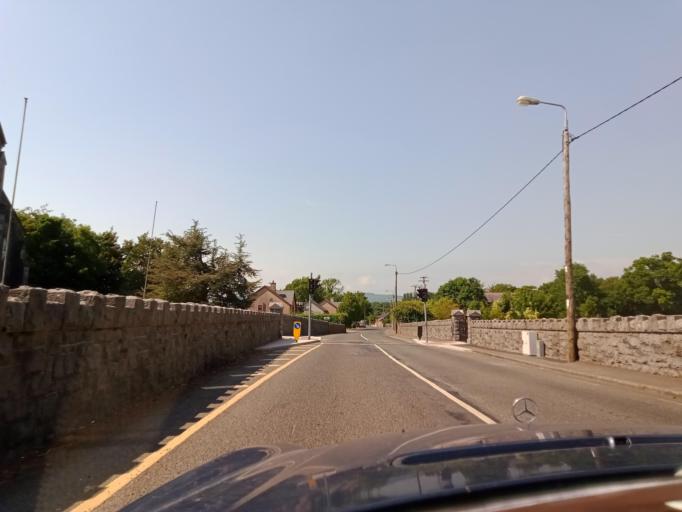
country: IE
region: Leinster
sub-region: Kilkenny
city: Piltown
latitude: 52.3463
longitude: -7.3223
